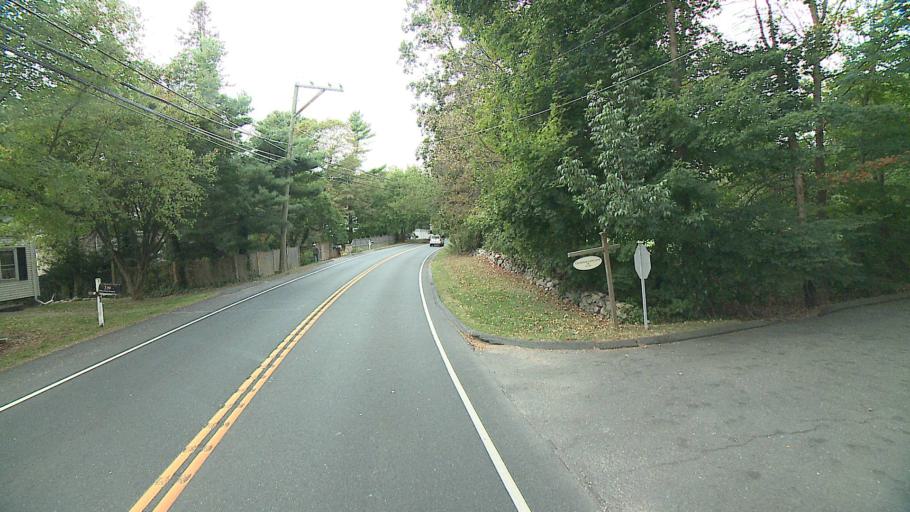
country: US
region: Connecticut
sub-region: Fairfield County
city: Westport
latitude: 41.1669
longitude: -73.3835
